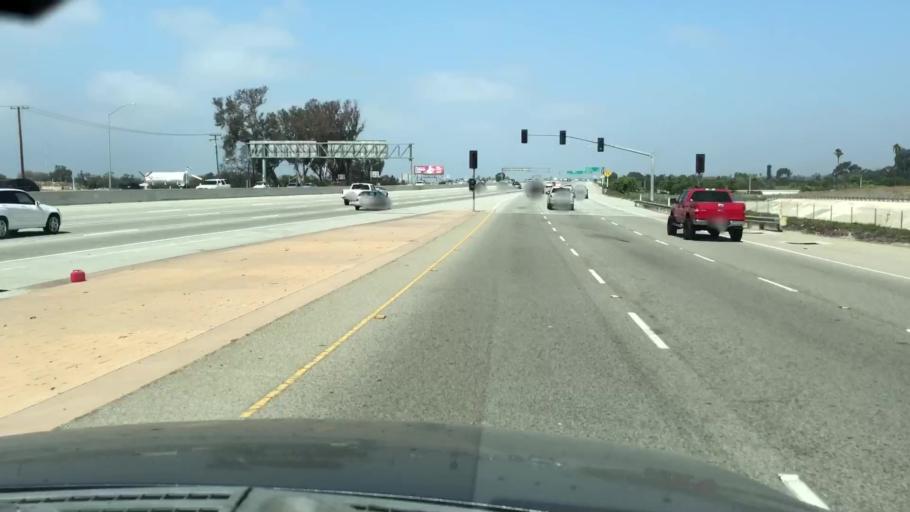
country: US
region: California
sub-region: Ventura County
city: El Rio
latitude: 34.2405
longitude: -119.1834
